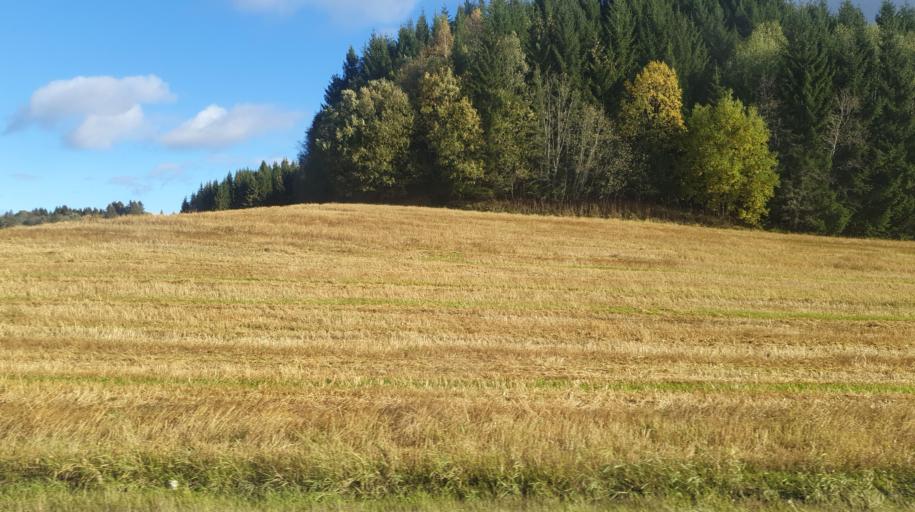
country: NO
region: Sor-Trondelag
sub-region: Klaebu
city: Klaebu
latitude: 63.3097
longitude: 10.4547
